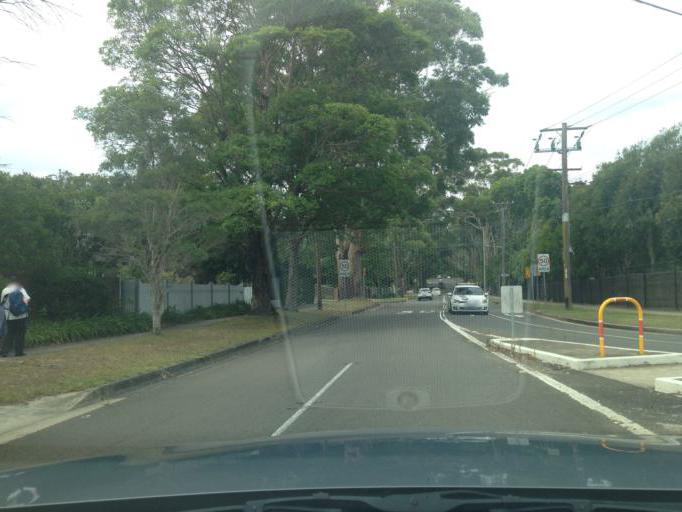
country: AU
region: New South Wales
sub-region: Ku-ring-gai
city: Killara
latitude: -33.7753
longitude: 151.1489
